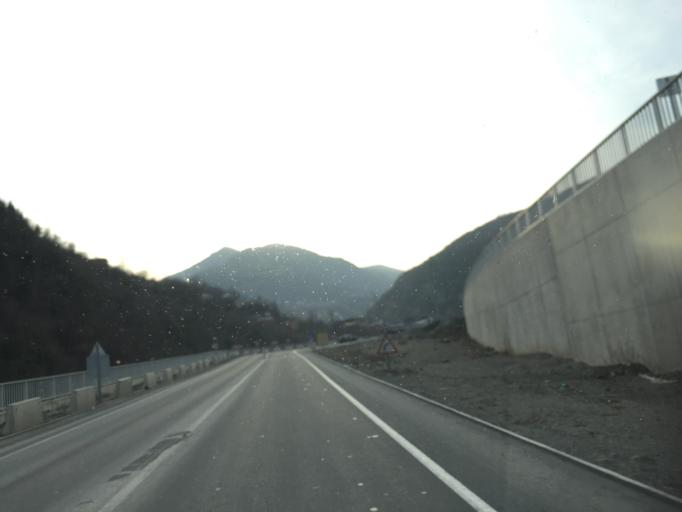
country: TR
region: Trabzon
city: Macka
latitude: 40.8047
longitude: 39.5951
